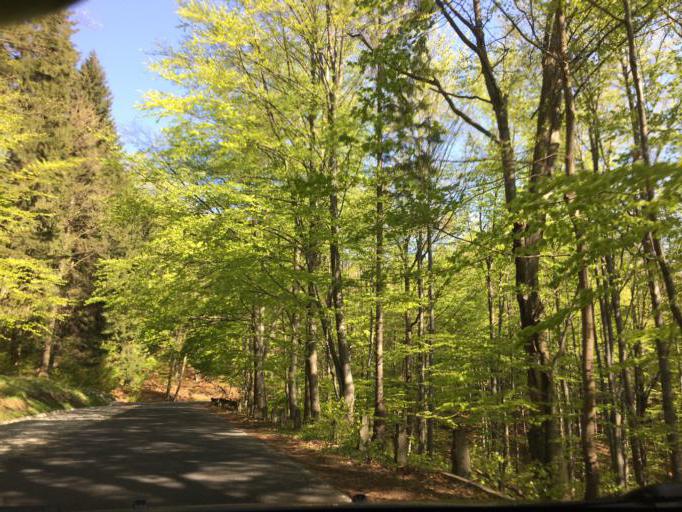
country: PL
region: Lower Silesian Voivodeship
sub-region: Powiat klodzki
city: Jugow
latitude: 50.6645
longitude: 16.5289
